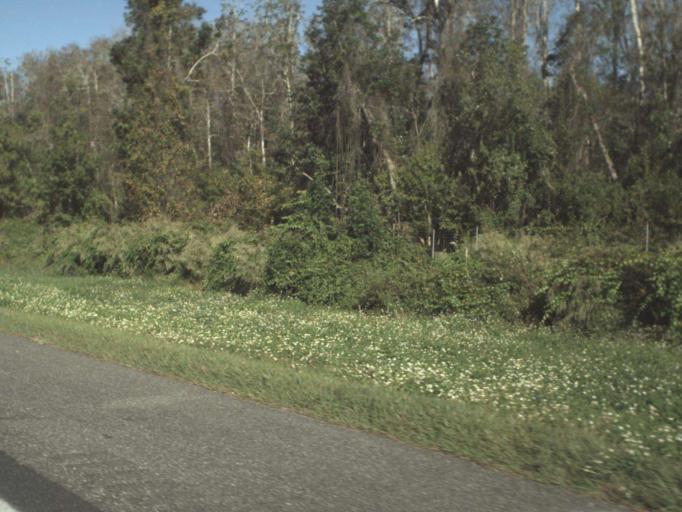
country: US
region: Florida
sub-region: Jefferson County
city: Monticello
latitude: 30.4659
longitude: -83.7987
